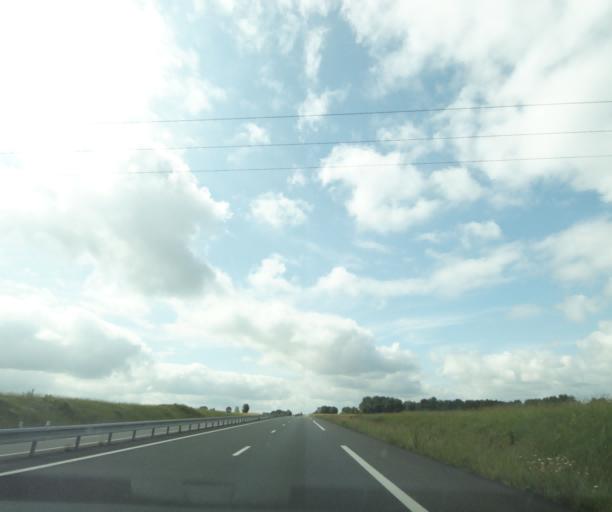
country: FR
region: Pays de la Loire
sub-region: Departement de Maine-et-Loire
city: Saint-Philbert-du-Peuple
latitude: 47.3662
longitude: -0.0835
